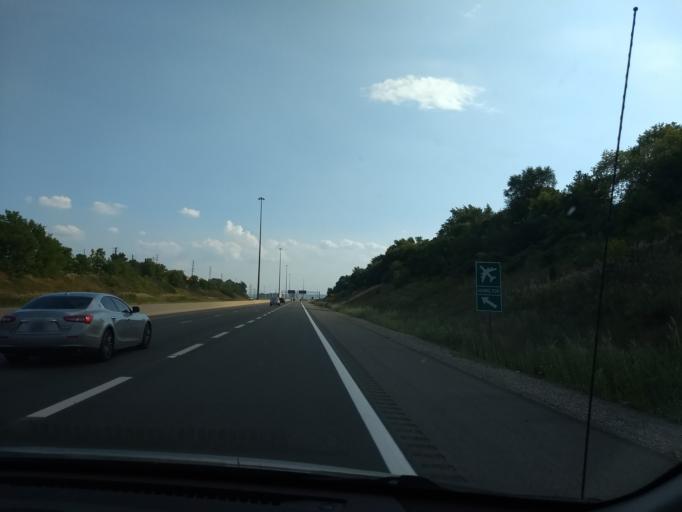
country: CA
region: Ontario
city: Burlington
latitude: 43.3474
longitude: -79.8314
